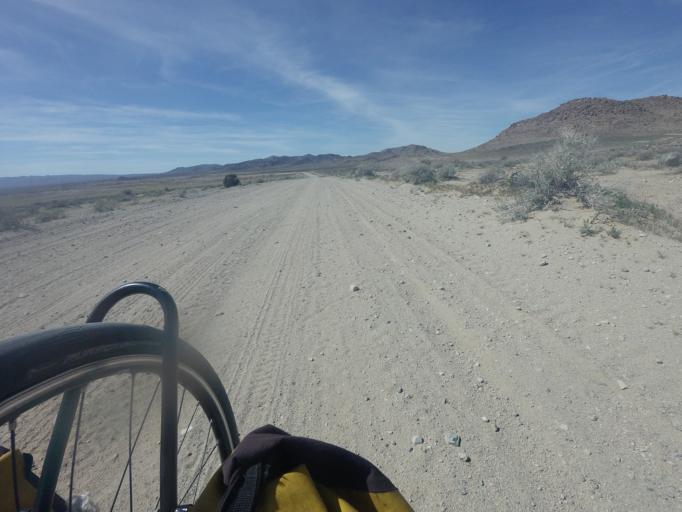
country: US
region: California
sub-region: San Bernardino County
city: Searles Valley
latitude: 35.6002
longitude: -117.3860
